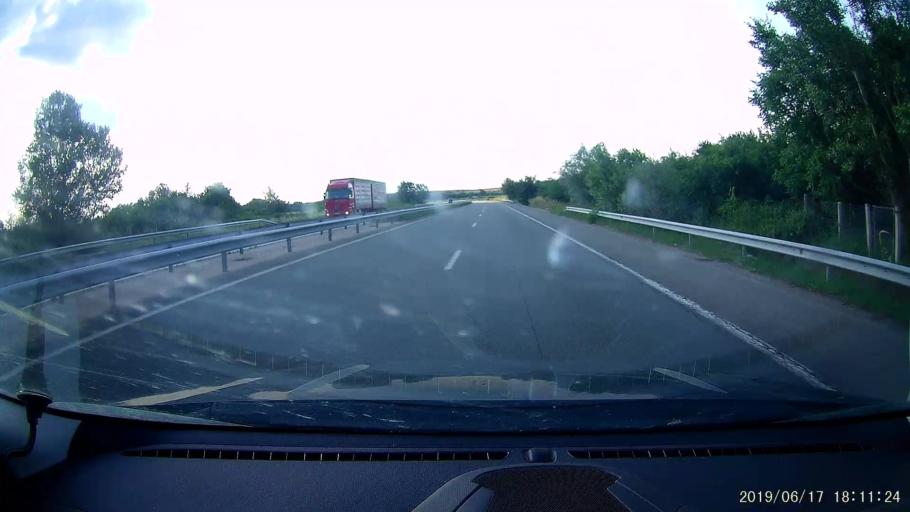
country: BG
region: Khaskovo
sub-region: Obshtina Lyubimets
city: Lyubimets
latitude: 41.8838
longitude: 26.0518
